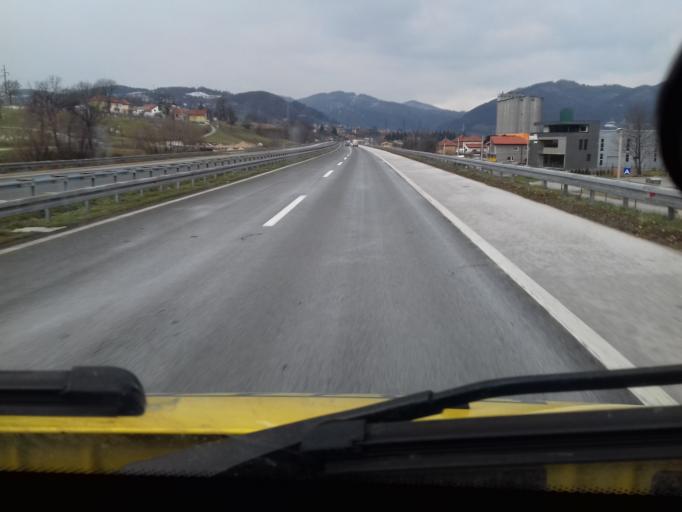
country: BA
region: Federation of Bosnia and Herzegovina
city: Dobrinje
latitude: 44.0286
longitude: 18.1300
